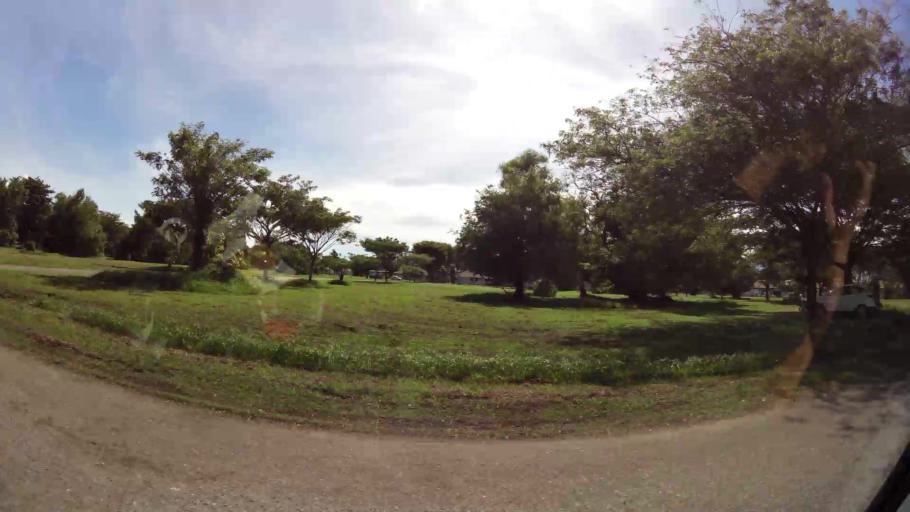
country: BN
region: Belait
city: Kuala Belait
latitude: 4.5877
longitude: 114.1997
